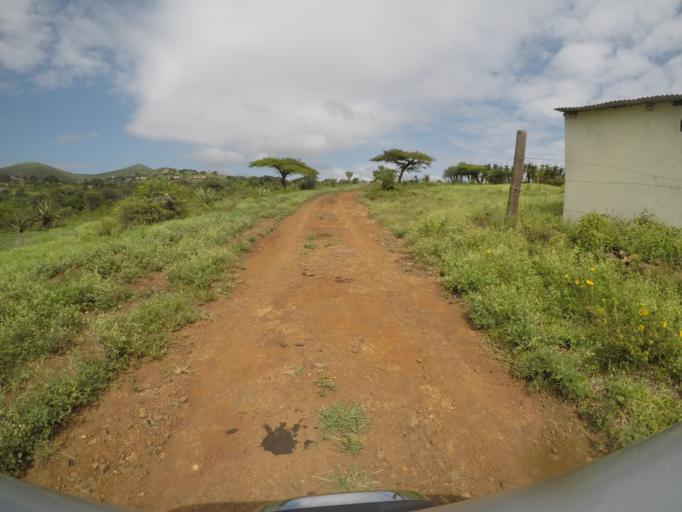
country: ZA
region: KwaZulu-Natal
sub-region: uThungulu District Municipality
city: Empangeni
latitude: -28.6210
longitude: 31.8737
